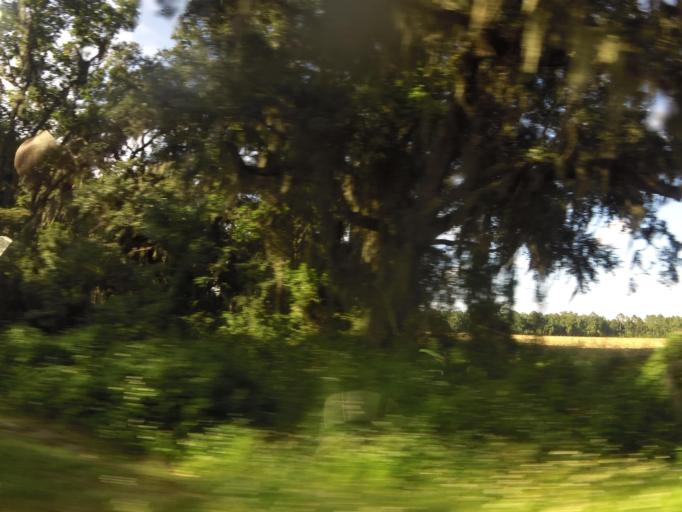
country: US
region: Florida
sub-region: Clay County
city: Green Cove Springs
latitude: 29.9171
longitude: -81.5769
